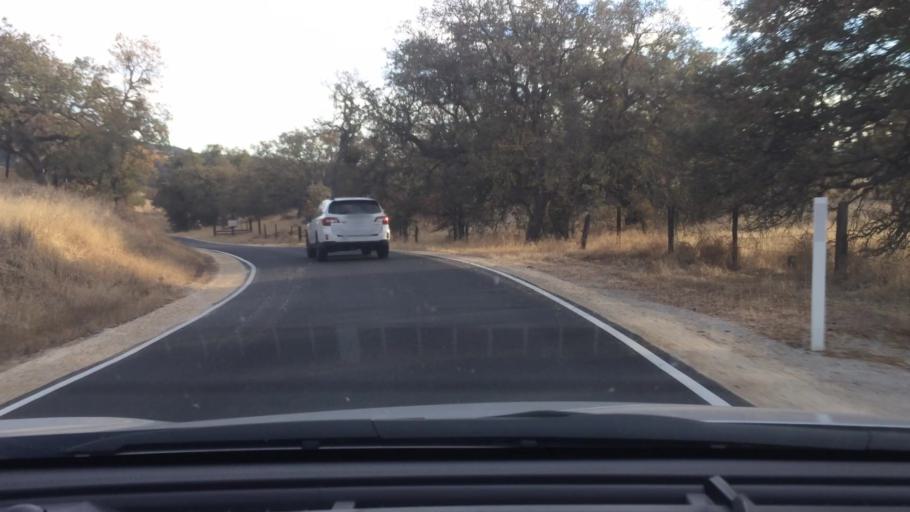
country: US
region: California
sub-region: Monterey County
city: Soledad
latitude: 36.4657
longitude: -121.2220
